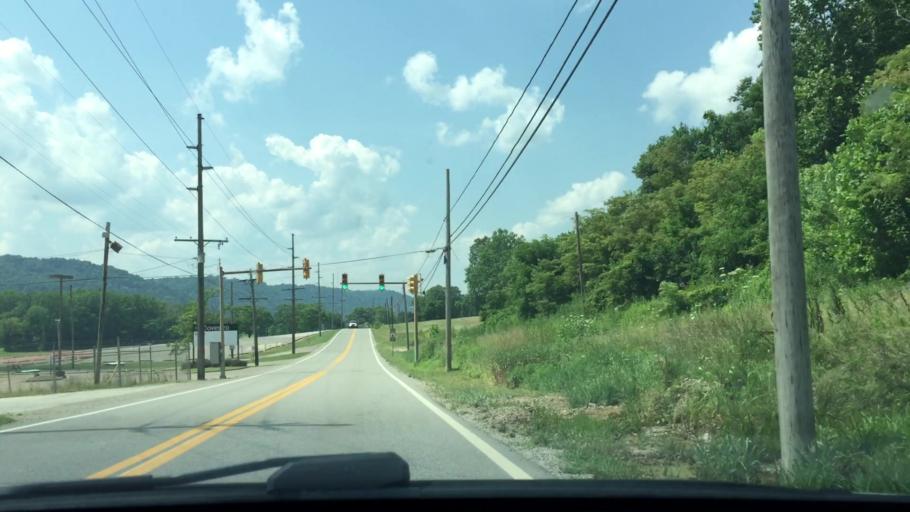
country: US
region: West Virginia
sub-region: Wetzel County
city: New Martinsville
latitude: 39.7315
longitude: -80.8325
